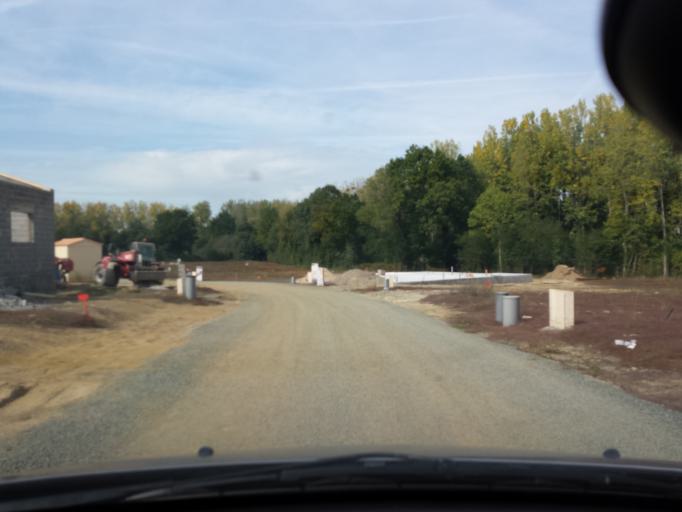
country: FR
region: Pays de la Loire
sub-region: Departement de la Vendee
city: Nieul-le-Dolent
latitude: 46.5720
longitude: -1.5122
